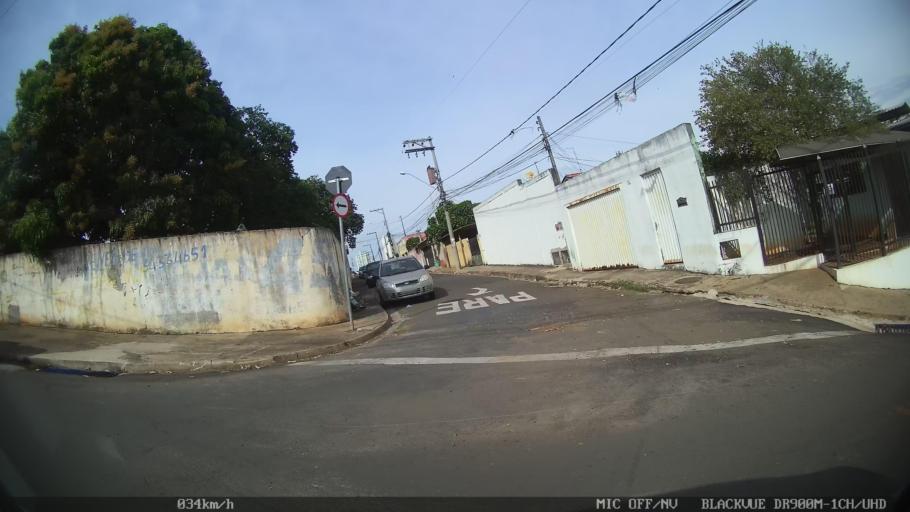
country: BR
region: Sao Paulo
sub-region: Piracicaba
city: Piracicaba
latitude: -22.7451
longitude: -47.6558
